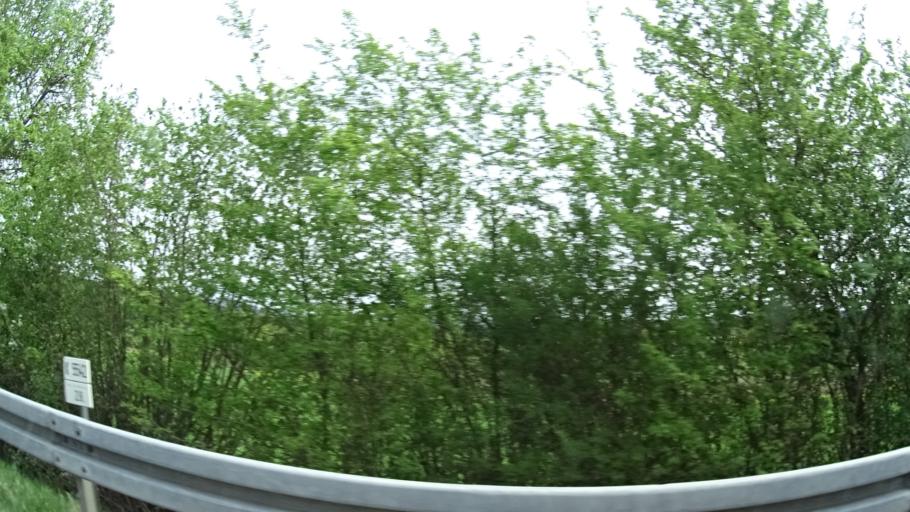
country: DE
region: Baden-Wuerttemberg
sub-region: Freiburg Region
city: Deisslingen
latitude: 48.1327
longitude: 8.6287
